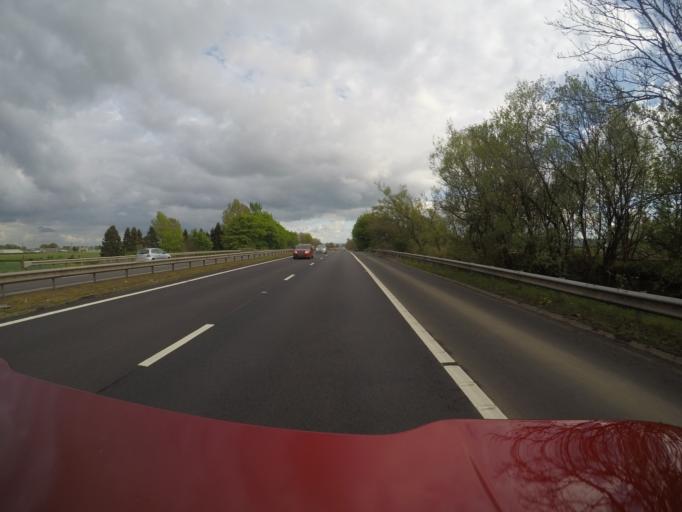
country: GB
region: Scotland
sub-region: Renfrewshire
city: Erskine
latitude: 55.8764
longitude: -4.4732
